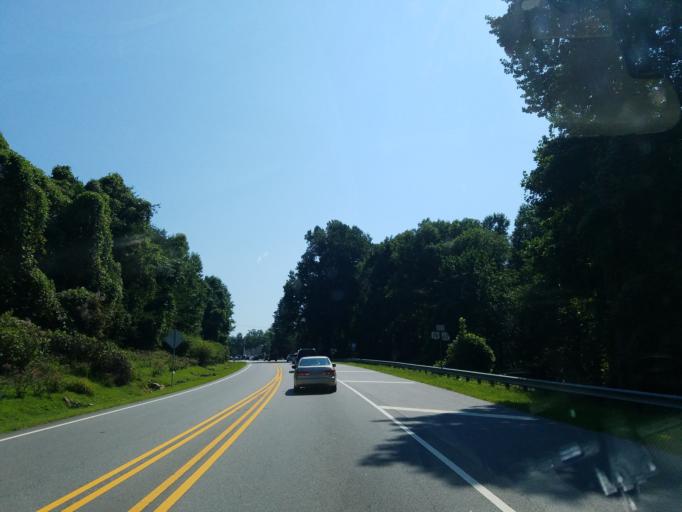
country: US
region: Georgia
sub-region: Lumpkin County
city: Dahlonega
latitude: 34.5392
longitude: -83.9753
